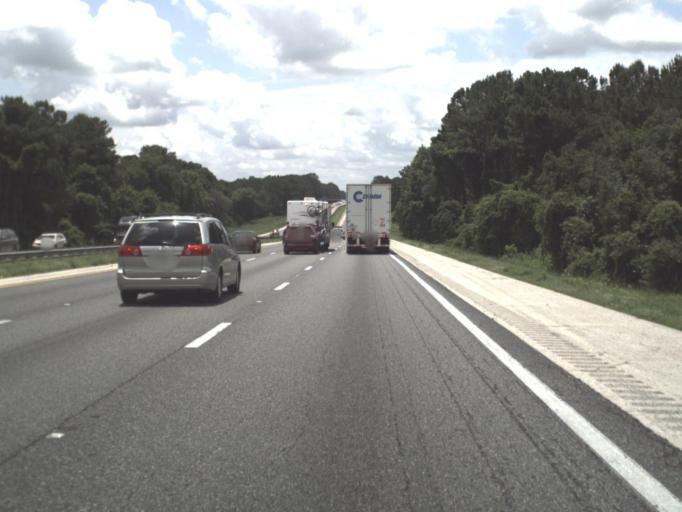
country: US
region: Florida
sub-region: Alachua County
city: High Springs
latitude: 29.8461
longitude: -82.5323
